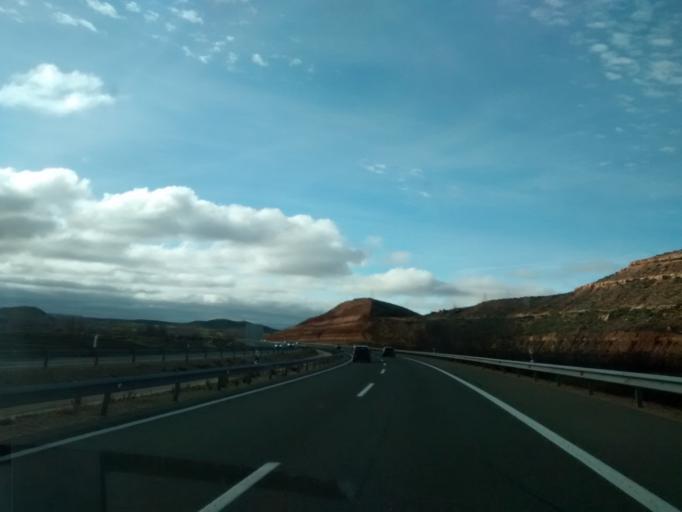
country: ES
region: Aragon
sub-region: Provincia de Zaragoza
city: Monreal de Ariza
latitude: 41.3054
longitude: -2.1402
